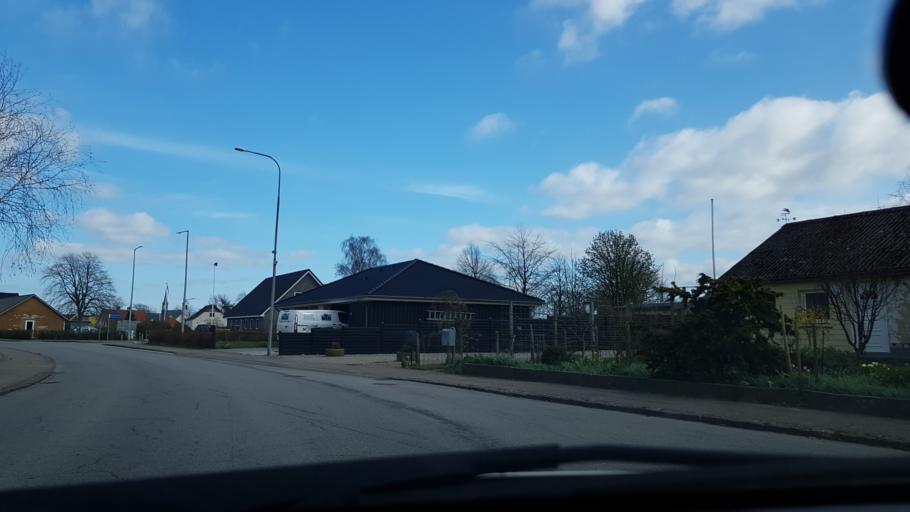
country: DK
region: South Denmark
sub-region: Vejen Kommune
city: Vejen
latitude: 55.4207
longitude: 9.1467
